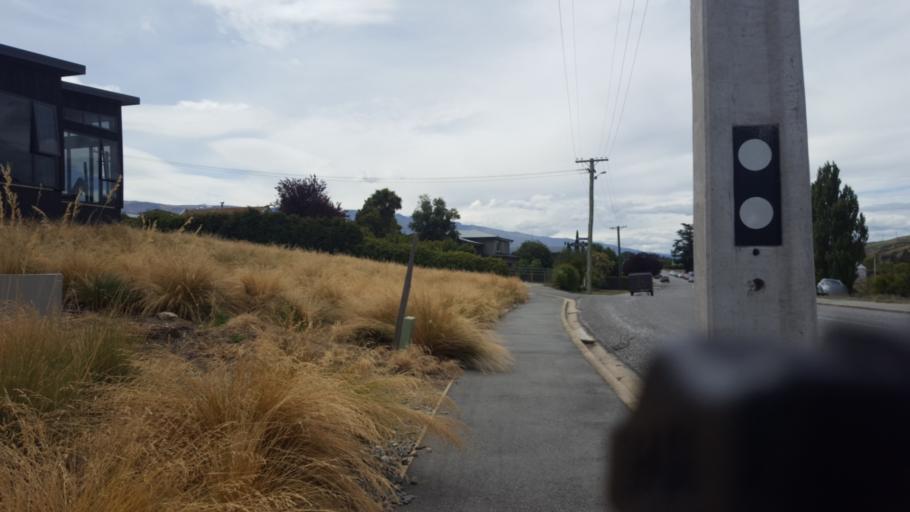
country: NZ
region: Otago
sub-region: Queenstown-Lakes District
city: Wanaka
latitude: -45.0483
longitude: 169.2116
